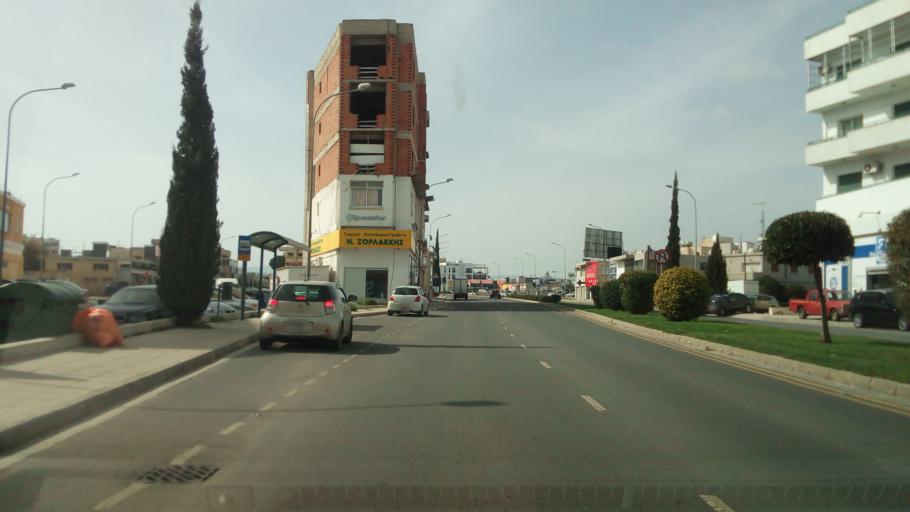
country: CY
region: Lefkosia
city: Nicosia
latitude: 35.1382
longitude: 33.3339
